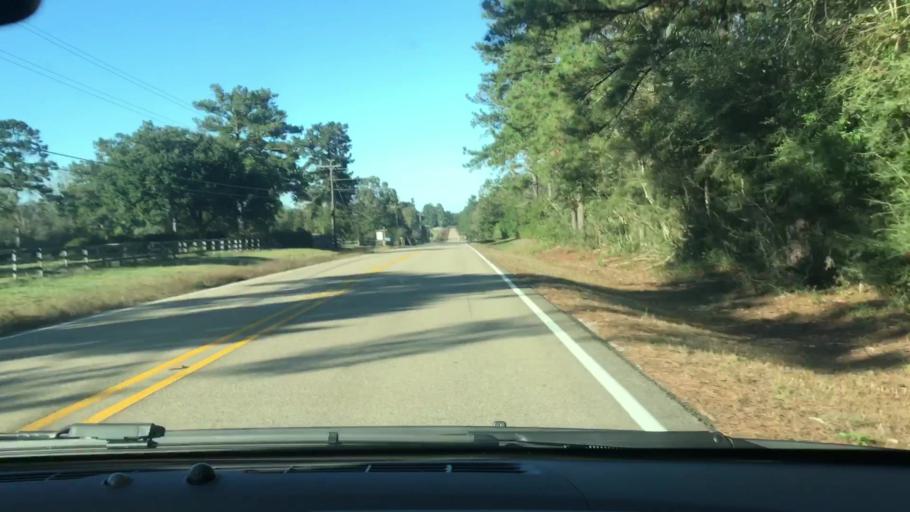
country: US
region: Louisiana
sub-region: Saint Tammany Parish
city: Abita Springs
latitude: 30.6288
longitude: -90.0165
